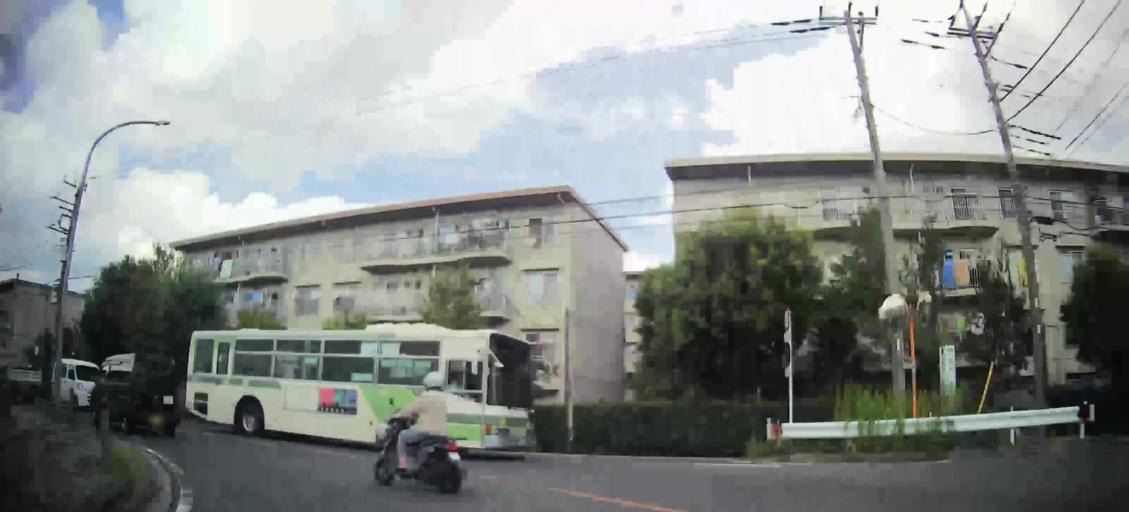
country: JP
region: Kanagawa
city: Yokohama
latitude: 35.4679
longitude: 139.5611
